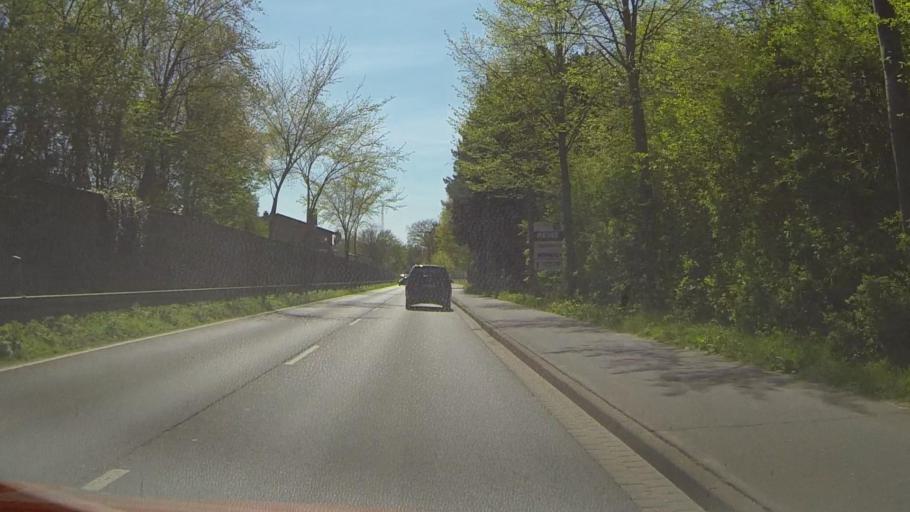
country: DE
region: Schleswig-Holstein
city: Tornesch
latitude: 53.6932
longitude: 9.7029
